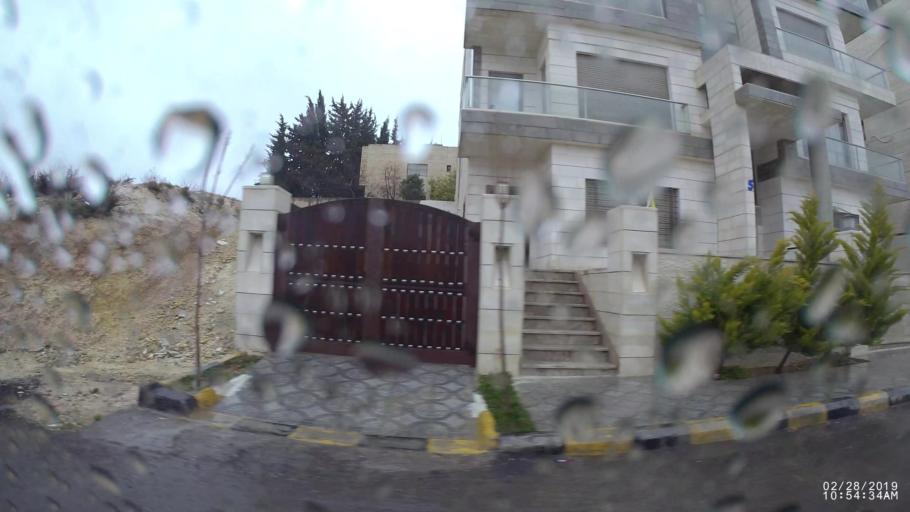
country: JO
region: Amman
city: Al Jubayhah
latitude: 32.0104
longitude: 35.8930
